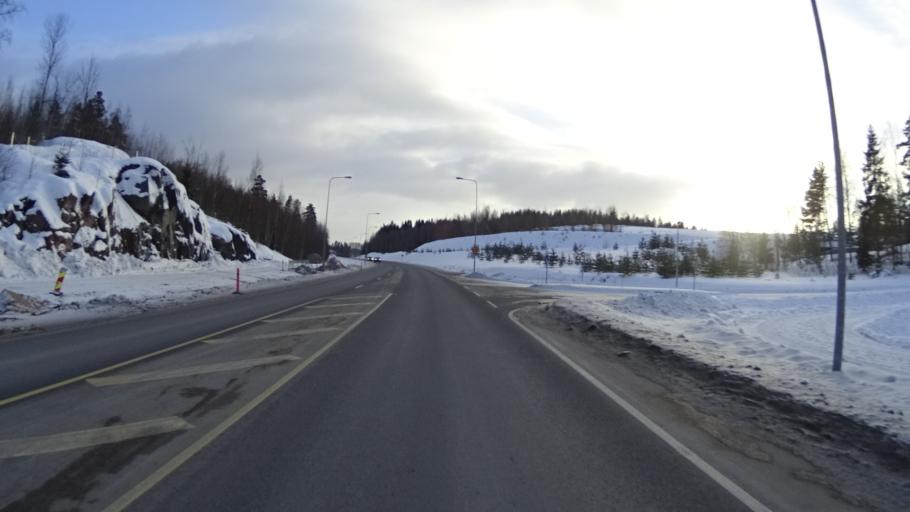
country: FI
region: Uusimaa
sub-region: Helsinki
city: Lohja
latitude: 60.2891
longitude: 24.0623
